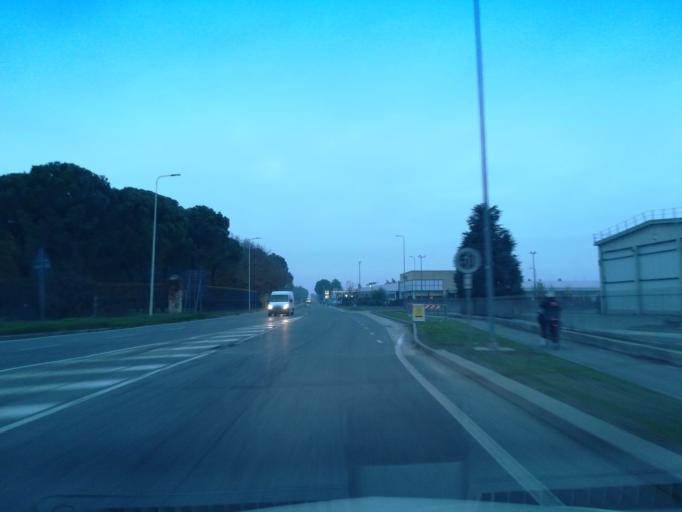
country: IT
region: Emilia-Romagna
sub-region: Provincia di Ravenna
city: Faenza
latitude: 44.2964
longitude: 11.8572
